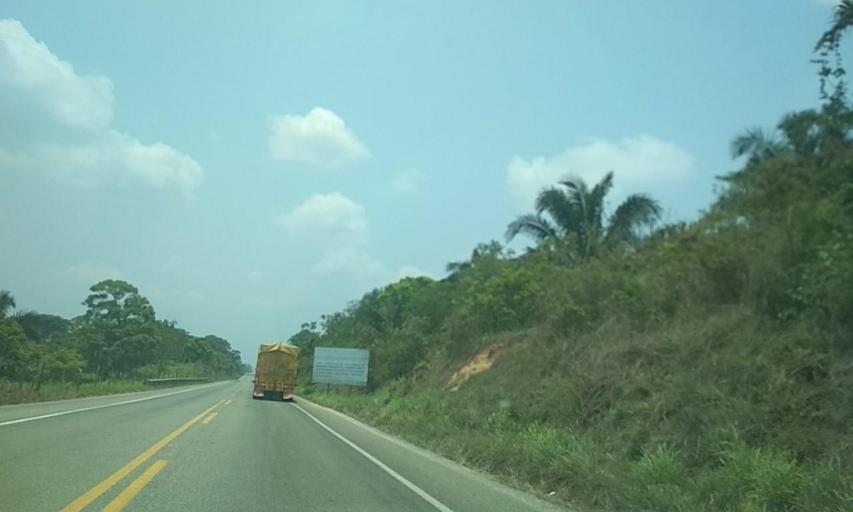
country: MX
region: Tabasco
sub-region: Huimanguillo
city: Francisco Rueda
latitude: 17.7277
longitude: -93.9638
